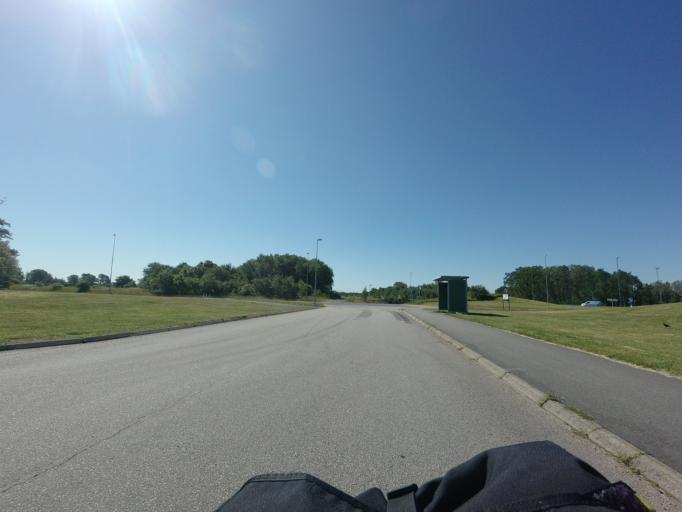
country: SE
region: Skane
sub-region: Hoganas Kommun
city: Hoganas
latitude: 56.1727
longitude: 12.5655
